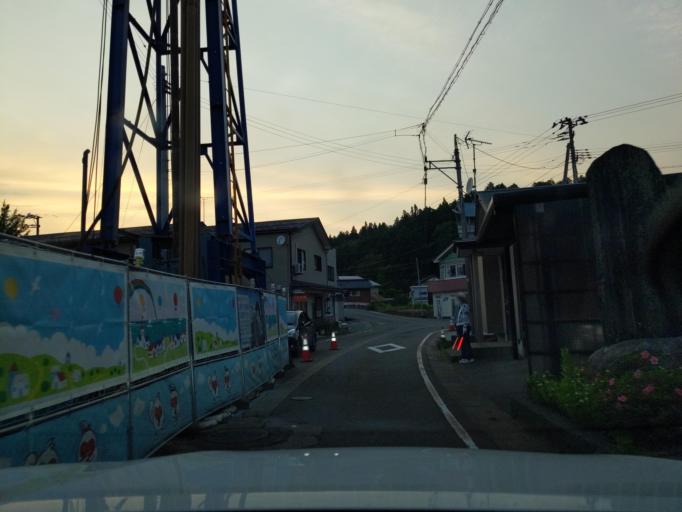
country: JP
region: Niigata
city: Kashiwazaki
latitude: 37.4485
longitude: 138.6402
